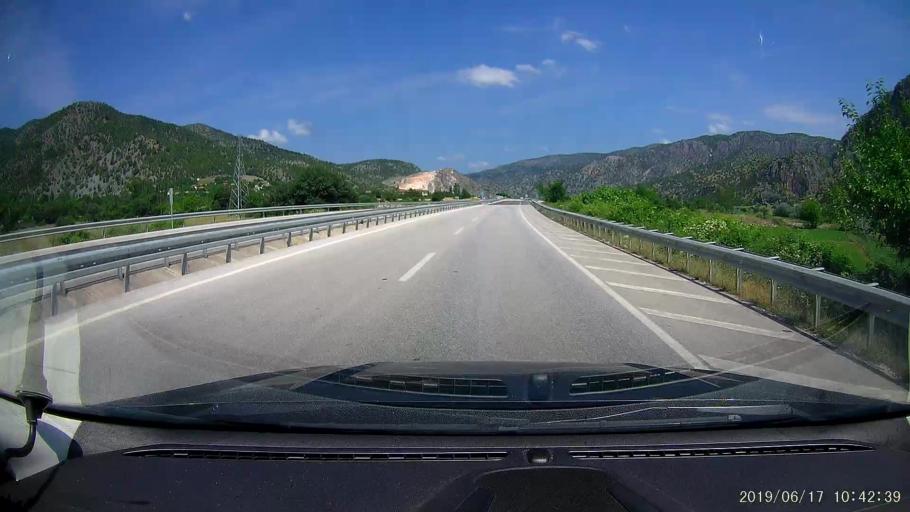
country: TR
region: Corum
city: Hacihamza
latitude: 41.0501
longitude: 34.5491
